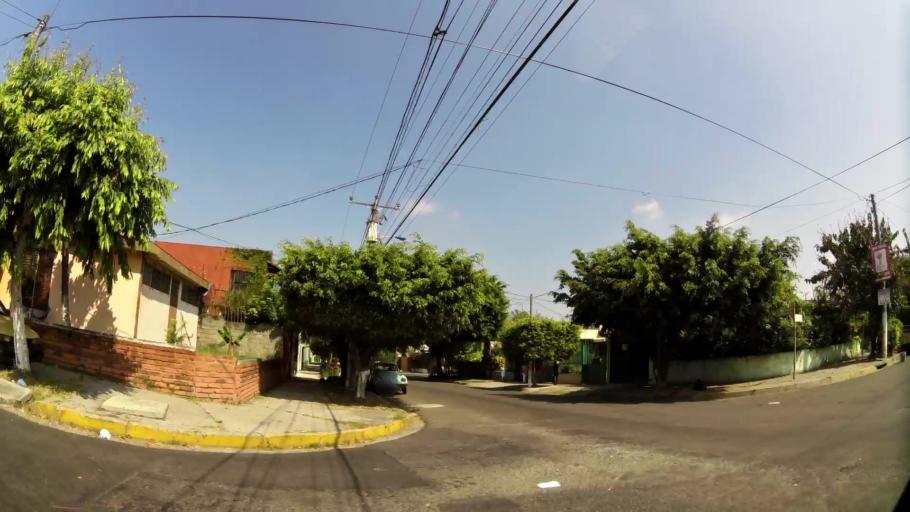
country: SV
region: San Salvador
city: San Salvador
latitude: 13.6862
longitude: -89.2217
